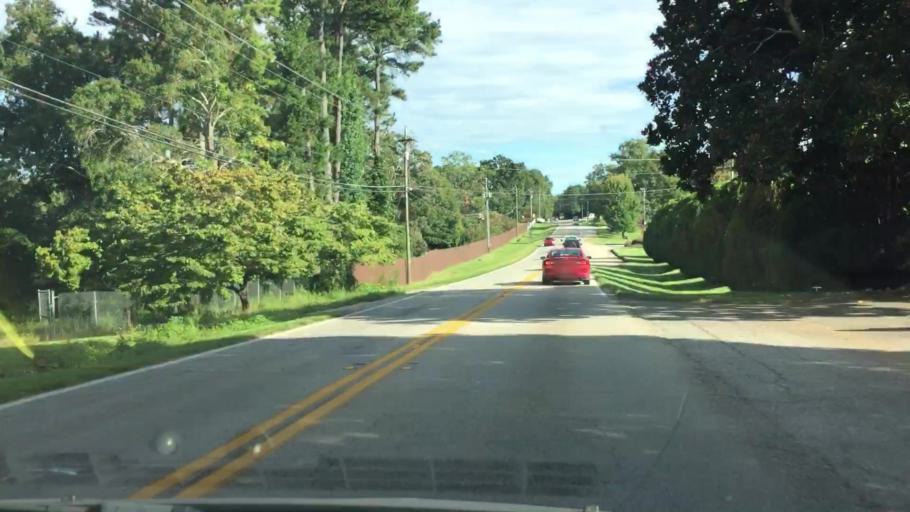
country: US
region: Georgia
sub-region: Henry County
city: Stockbridge
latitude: 33.6138
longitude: -84.2304
